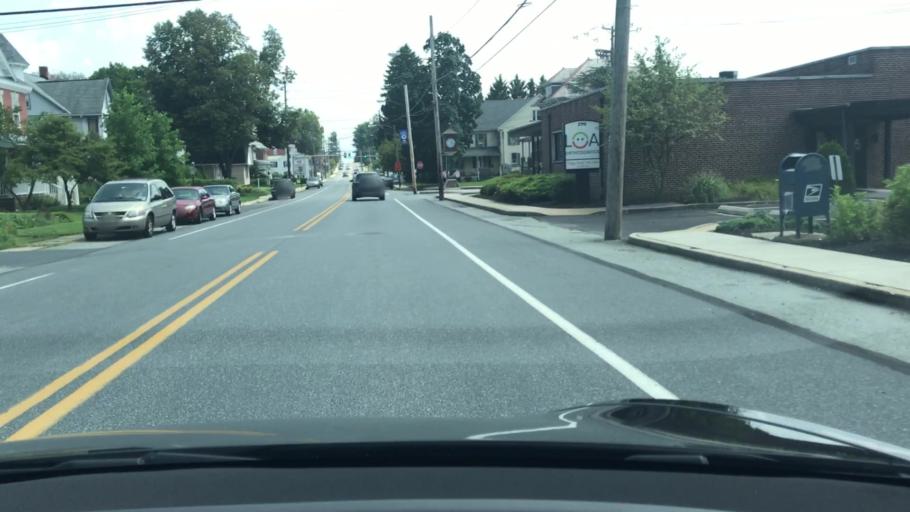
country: US
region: Pennsylvania
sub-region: Lancaster County
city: Landisville
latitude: 40.0960
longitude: -76.4123
